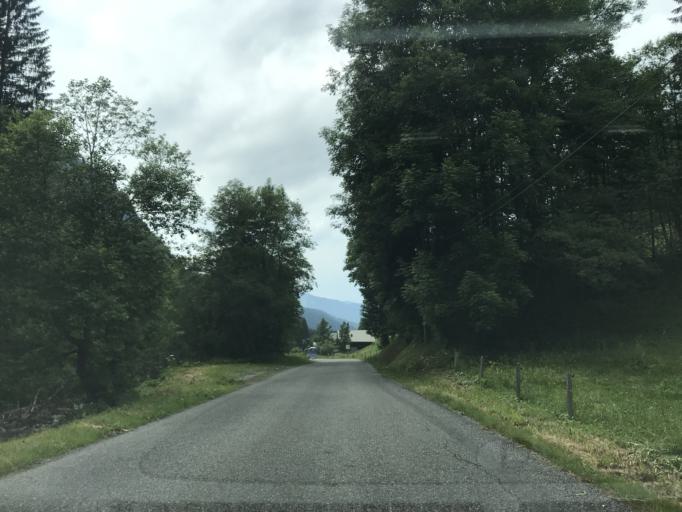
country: FR
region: Rhone-Alpes
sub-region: Departement de la Haute-Savoie
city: Morzine
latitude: 46.1530
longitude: 6.7392
